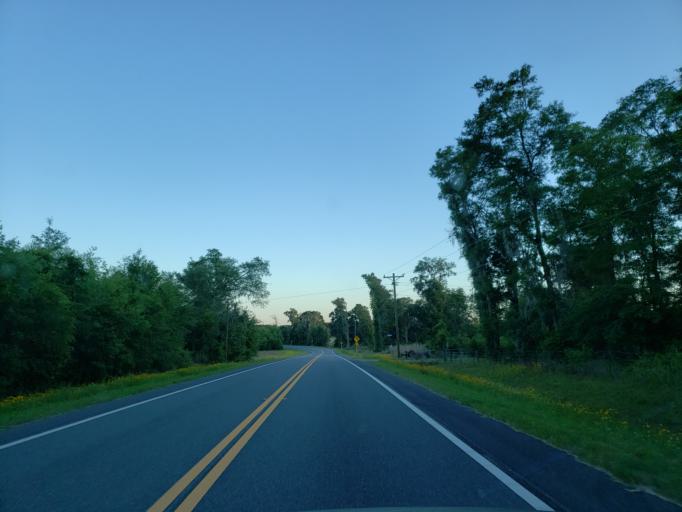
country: US
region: Florida
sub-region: Madison County
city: Madison
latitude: 30.5857
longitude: -83.2414
